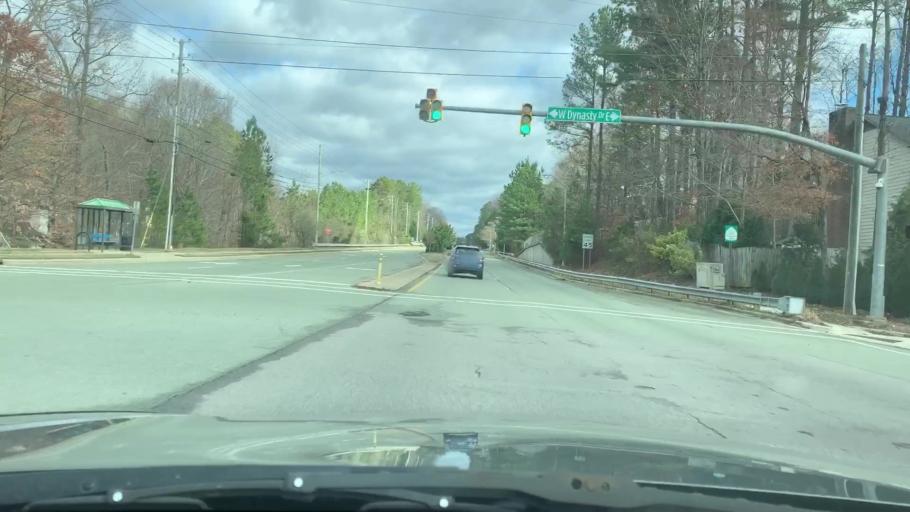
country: US
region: North Carolina
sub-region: Wake County
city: Cary
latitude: 35.8098
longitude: -78.7811
